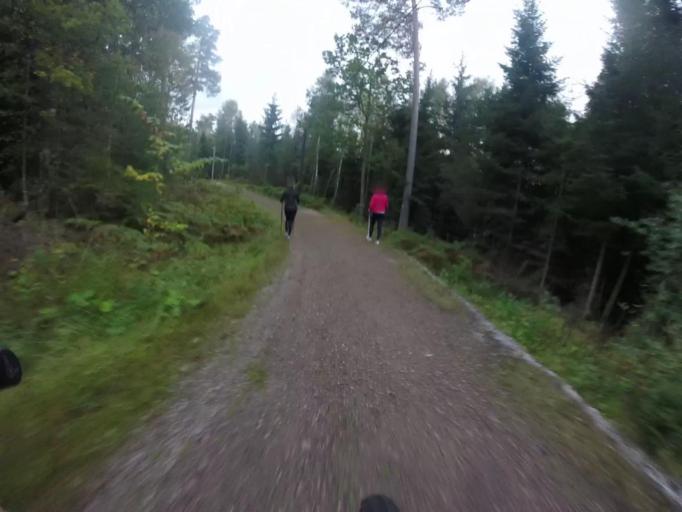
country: SE
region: Vaestra Goetaland
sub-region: Trollhattan
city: Trollhattan
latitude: 58.2898
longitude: 12.2558
